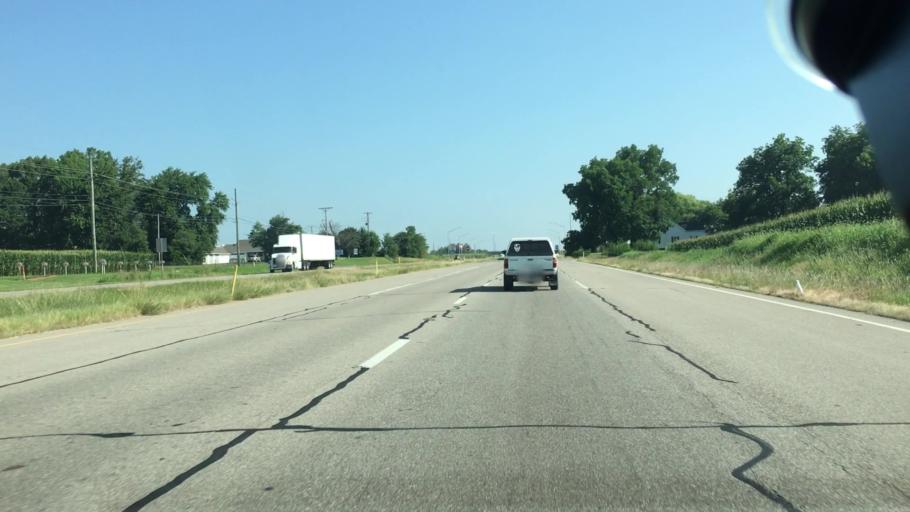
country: US
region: Indiana
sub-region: Gibson County
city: Fort Branch
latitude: 38.2657
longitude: -87.5677
